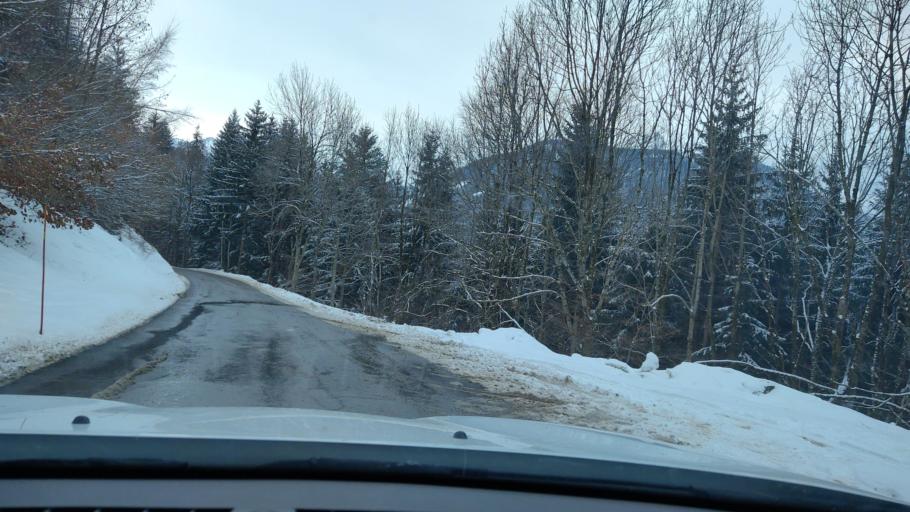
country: FR
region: Rhone-Alpes
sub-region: Departement de la Savoie
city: Beaufort
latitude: 45.7326
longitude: 6.5731
